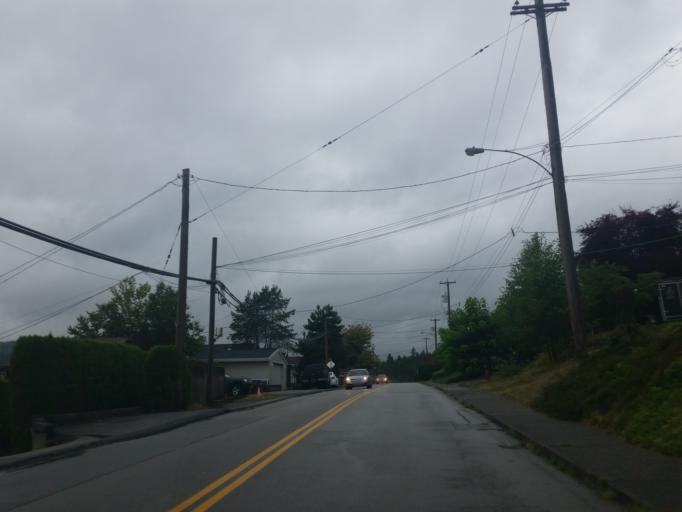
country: CA
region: British Columbia
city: Port Moody
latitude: 49.2951
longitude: -122.8588
